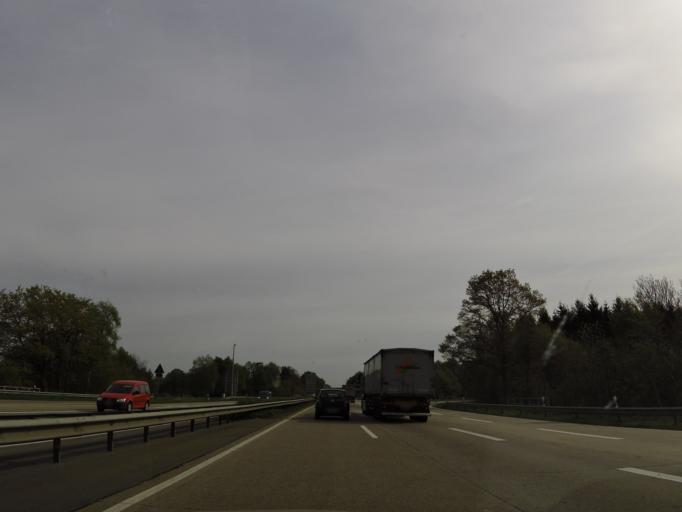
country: DE
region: Lower Saxony
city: Bad Fallingbostel
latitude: 52.8885
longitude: 9.7640
